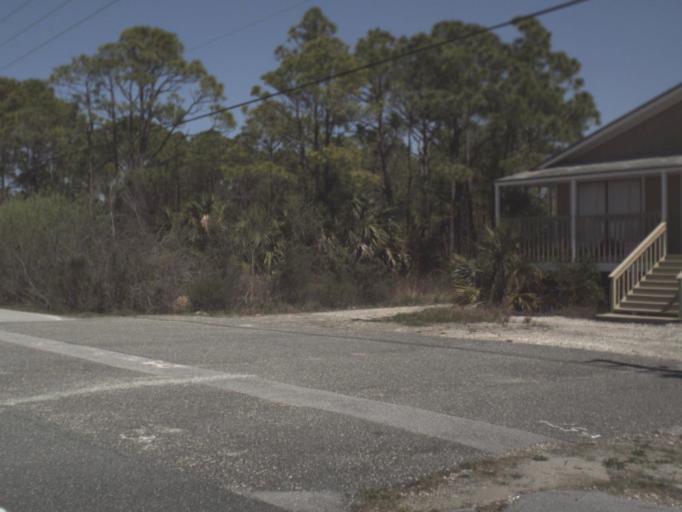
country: US
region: Florida
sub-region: Gulf County
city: Port Saint Joe
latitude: 29.7374
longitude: -85.3934
